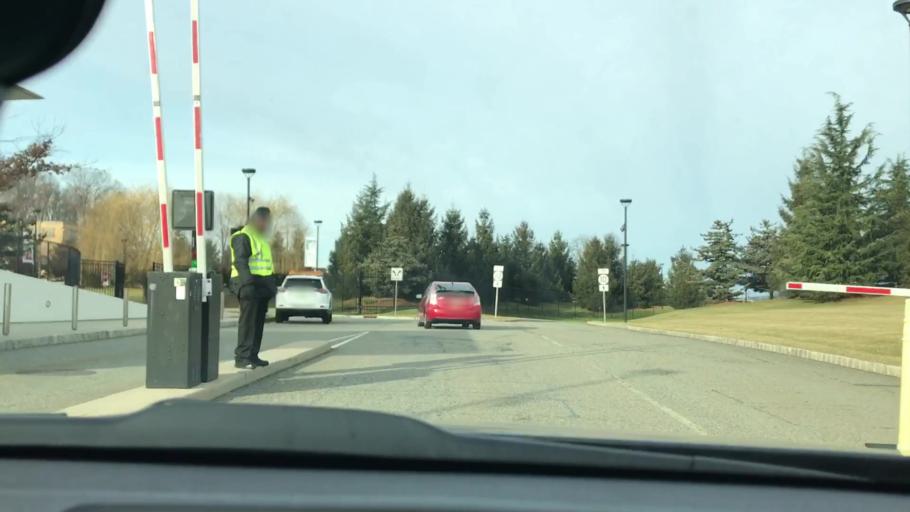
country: US
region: New Jersey
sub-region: Morris County
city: Hanover
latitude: 40.8103
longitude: -74.3850
